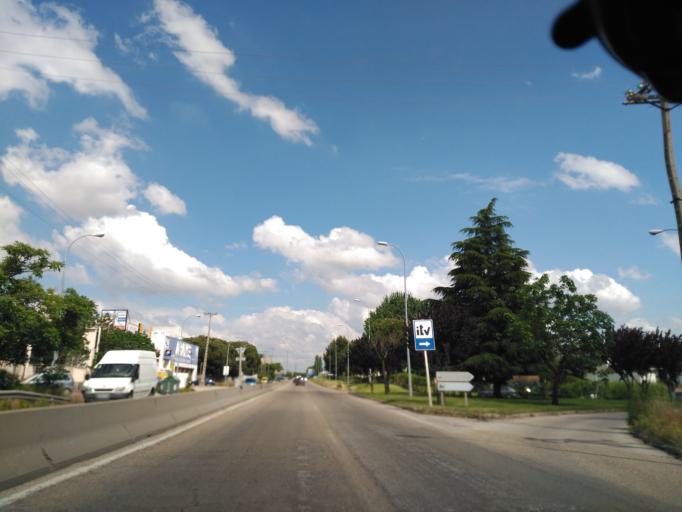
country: ES
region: Madrid
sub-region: Provincia de Madrid
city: Getafe
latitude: 40.3040
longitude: -3.6999
